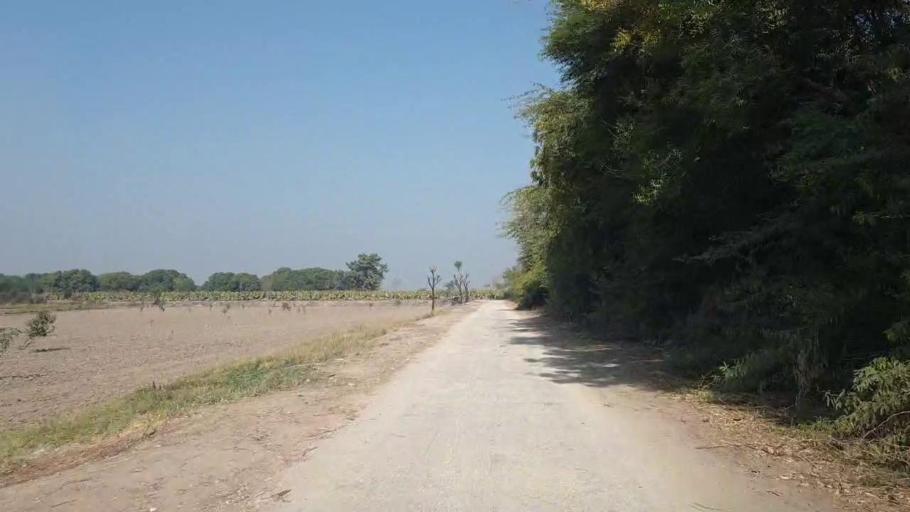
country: PK
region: Sindh
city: Chambar
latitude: 25.3472
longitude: 68.8516
